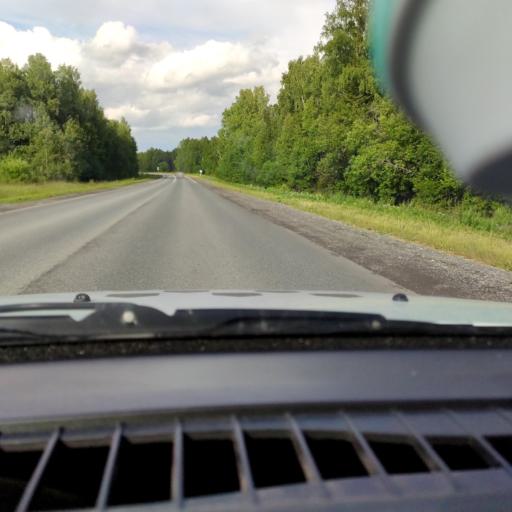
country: RU
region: Perm
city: Orda
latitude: 57.2466
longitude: 56.9940
